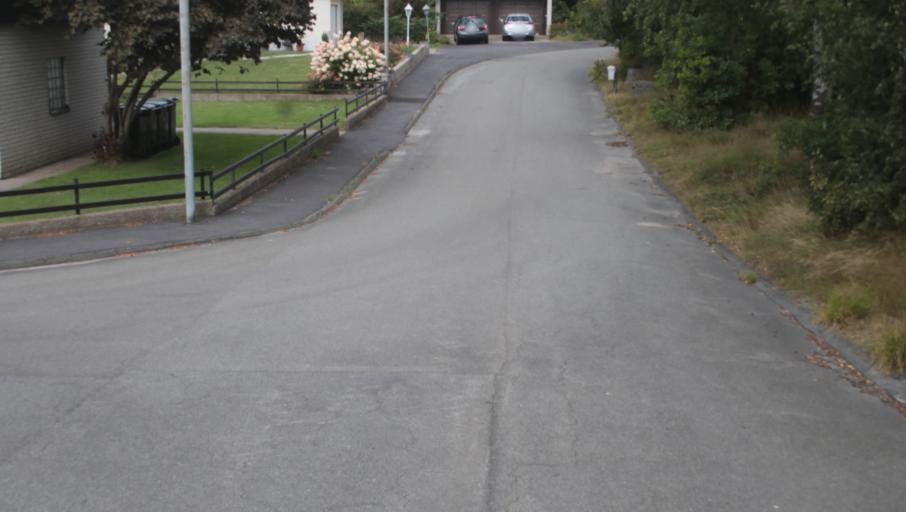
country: SE
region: Blekinge
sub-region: Karlshamns Kommun
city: Karlshamn
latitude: 56.1734
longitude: 14.8530
